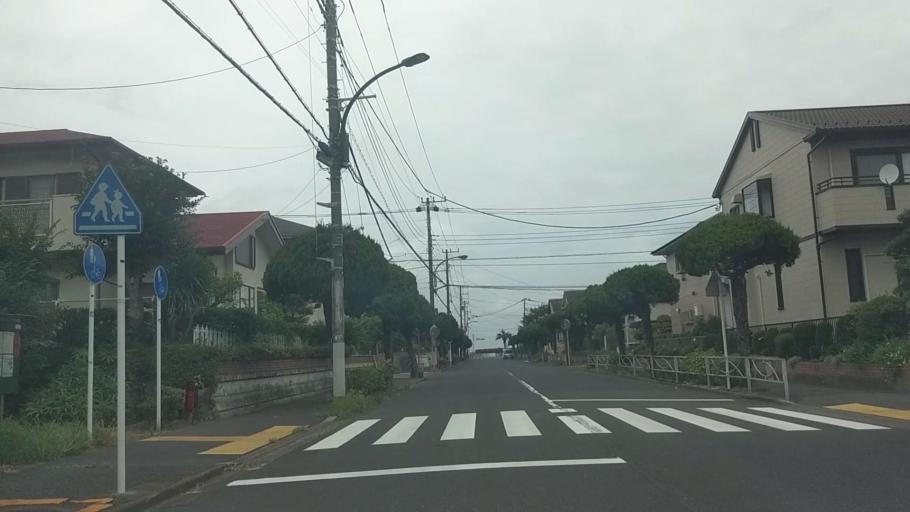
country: JP
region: Kanagawa
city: Yokosuka
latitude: 35.2616
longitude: 139.7082
